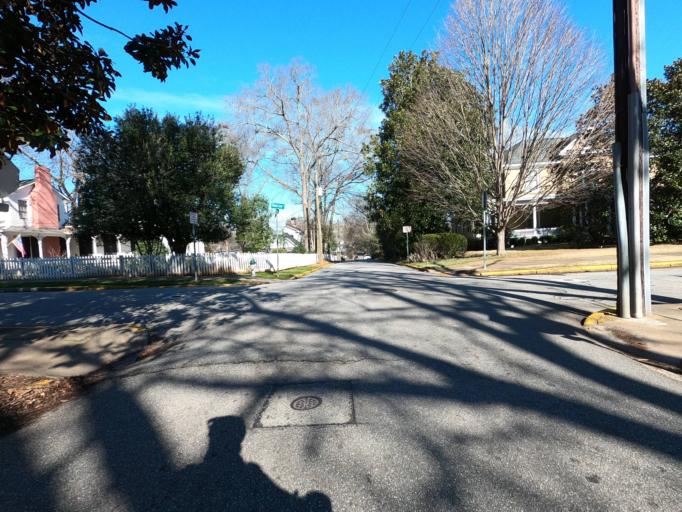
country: US
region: Georgia
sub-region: Clarke County
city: Athens
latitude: 33.9544
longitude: -83.3852
